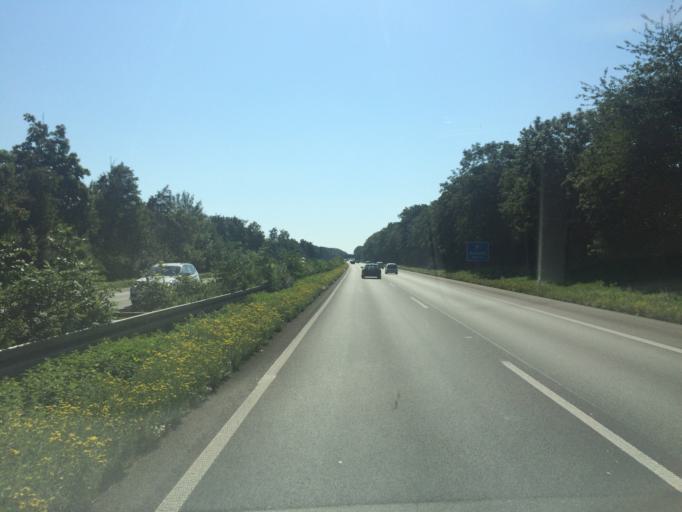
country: DE
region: North Rhine-Westphalia
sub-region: Regierungsbezirk Munster
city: Ascheberg
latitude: 51.7573
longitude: 7.6439
